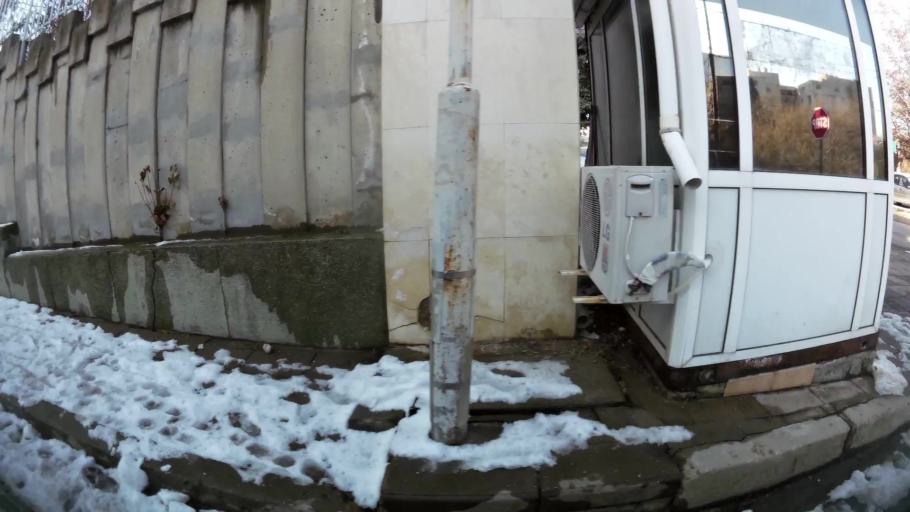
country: BG
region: Sofia-Capital
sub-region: Stolichna Obshtina
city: Sofia
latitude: 42.6700
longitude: 23.3454
